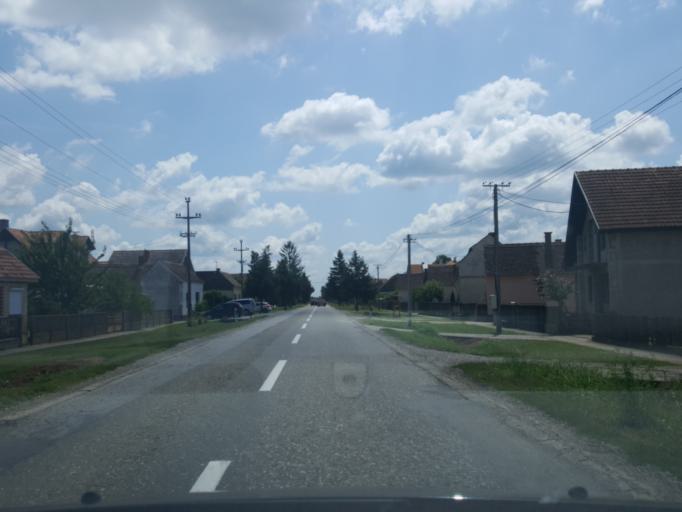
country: RS
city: Glusci
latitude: 44.8861
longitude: 19.5518
